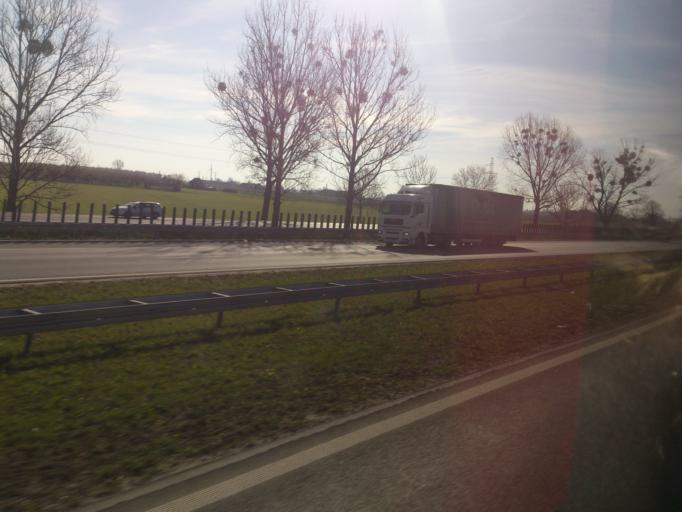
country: PL
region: Kujawsko-Pomorskie
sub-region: Powiat aleksandrowski
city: Raciazek
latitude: 52.8379
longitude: 18.7956
